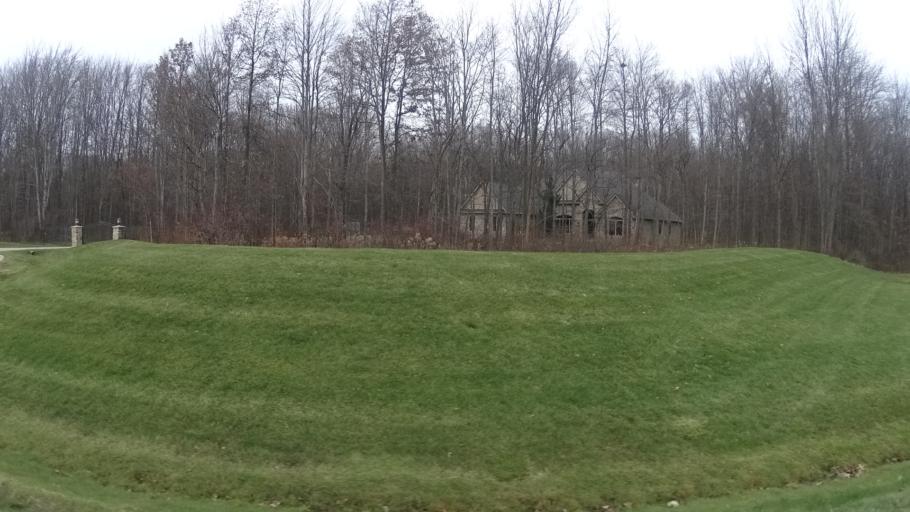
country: US
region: Ohio
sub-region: Lorain County
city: Eaton Estates
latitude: 41.2796
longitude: -81.9633
